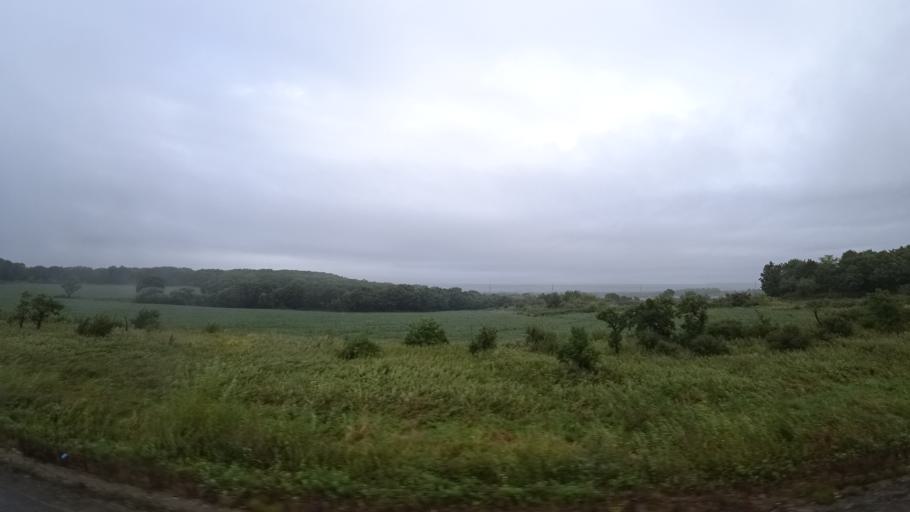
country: RU
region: Primorskiy
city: Monastyrishche
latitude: 44.2720
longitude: 132.4685
